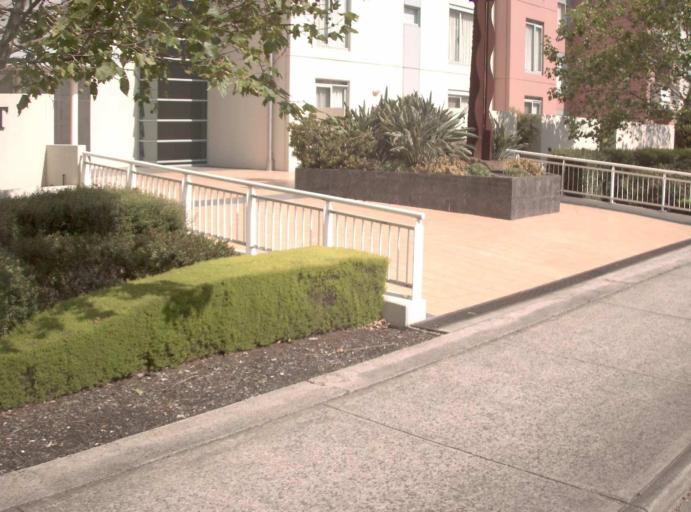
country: AU
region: Victoria
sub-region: Manningham
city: Doncaster
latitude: -37.7840
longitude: 145.1241
